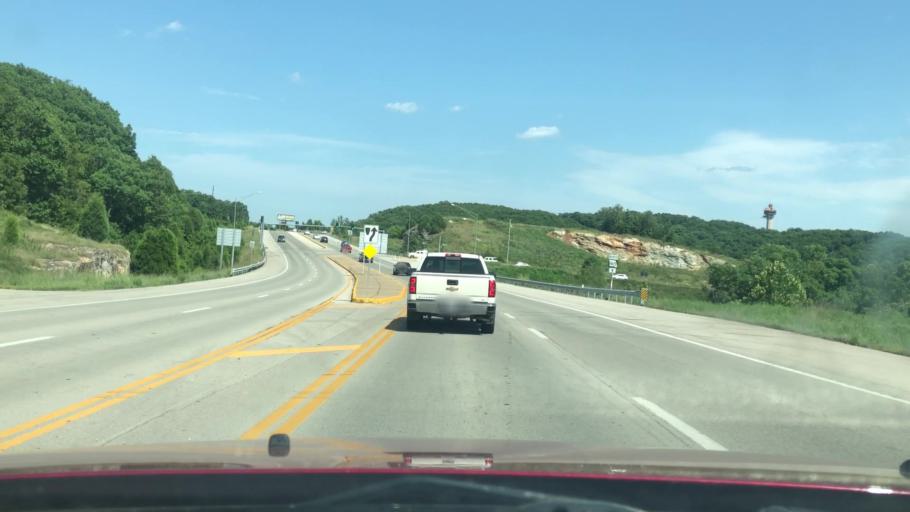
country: US
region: Missouri
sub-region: Stone County
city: Kimberling City
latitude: 36.6760
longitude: -93.3219
